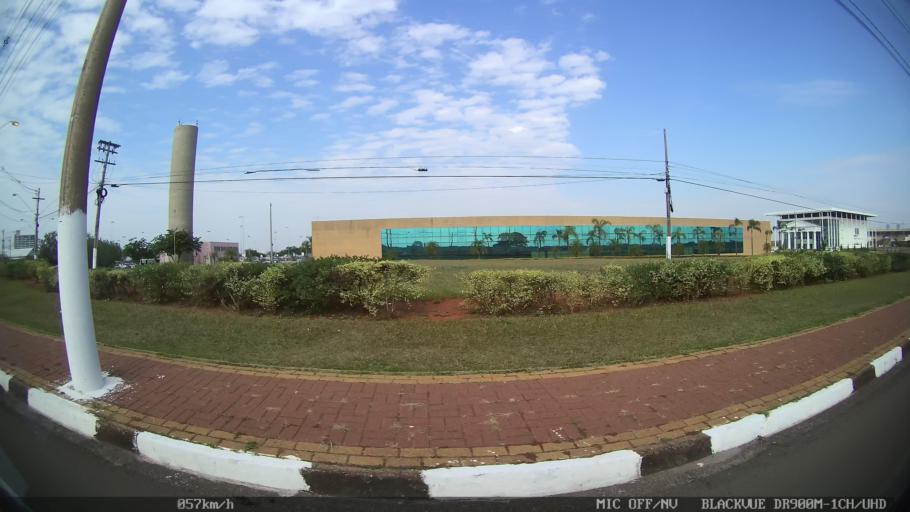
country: BR
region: Sao Paulo
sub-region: Paulinia
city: Paulinia
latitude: -22.7833
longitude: -47.1590
